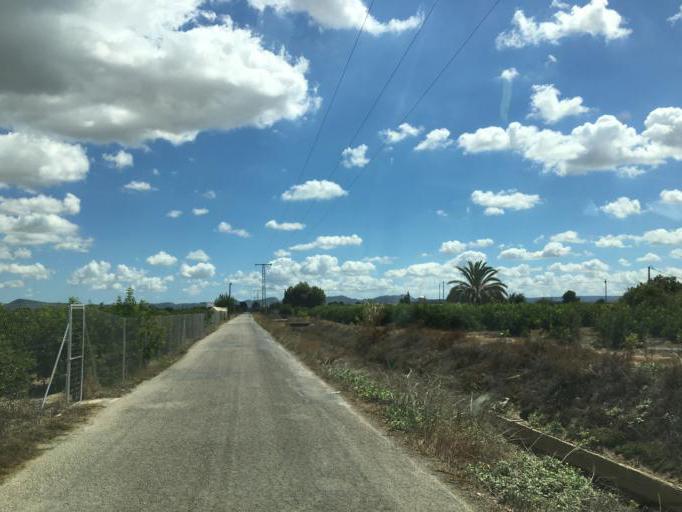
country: ES
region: Murcia
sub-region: Murcia
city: Santomera
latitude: 38.0490
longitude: -1.0492
